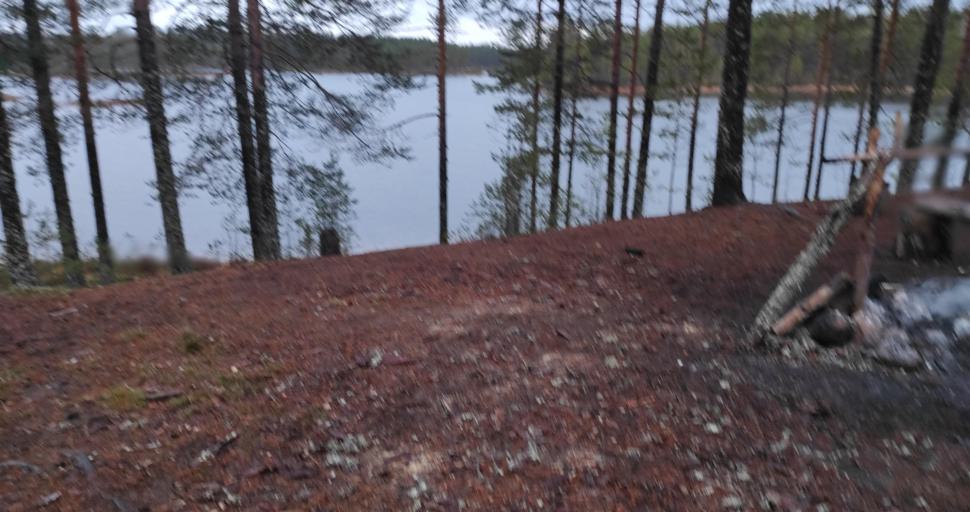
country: RU
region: Republic of Karelia
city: Salmi
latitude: 61.6256
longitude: 31.8108
